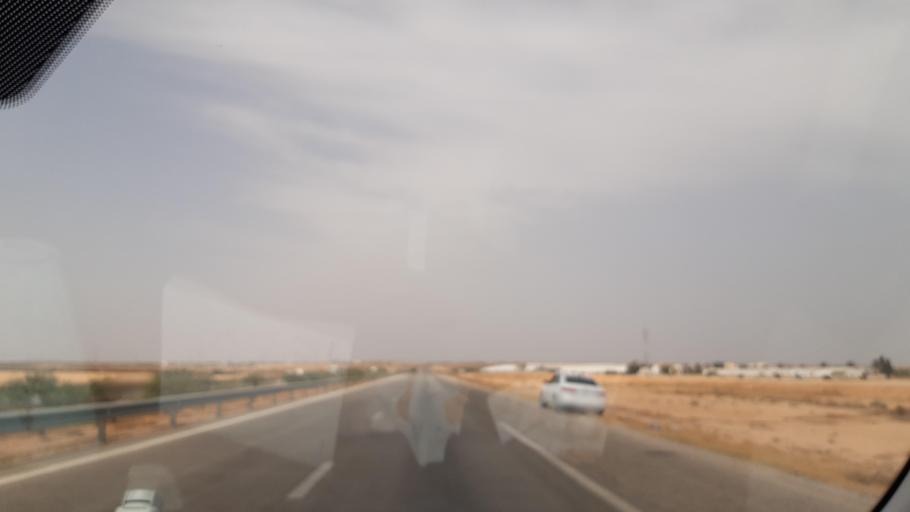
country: TN
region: Safaqis
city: Sfax
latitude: 34.7720
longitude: 10.6108
